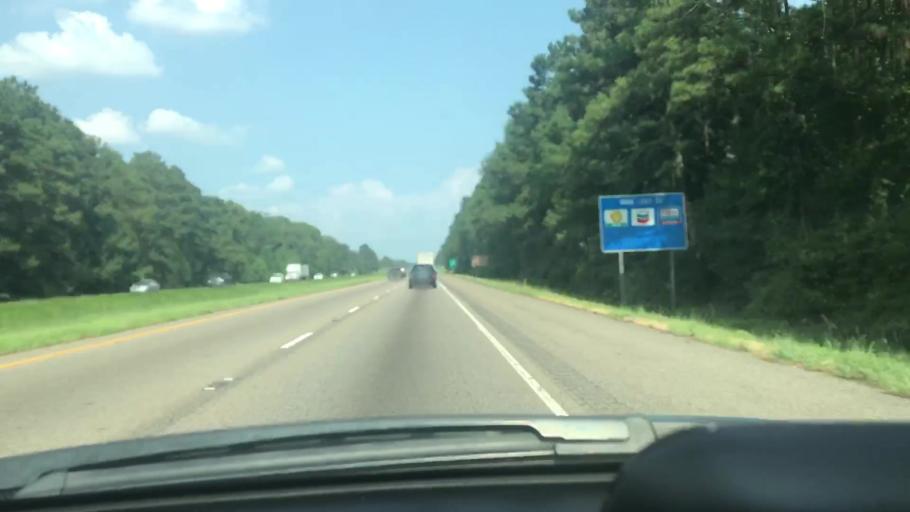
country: US
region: Louisiana
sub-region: Livingston Parish
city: Albany
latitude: 30.4769
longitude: -90.5885
